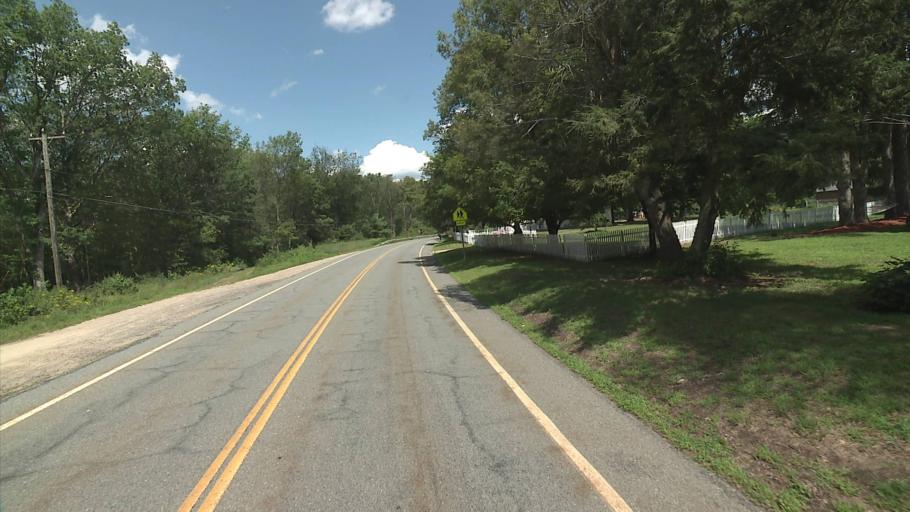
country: US
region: Connecticut
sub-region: Tolland County
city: Mansfield City
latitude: 41.7722
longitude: -72.1947
